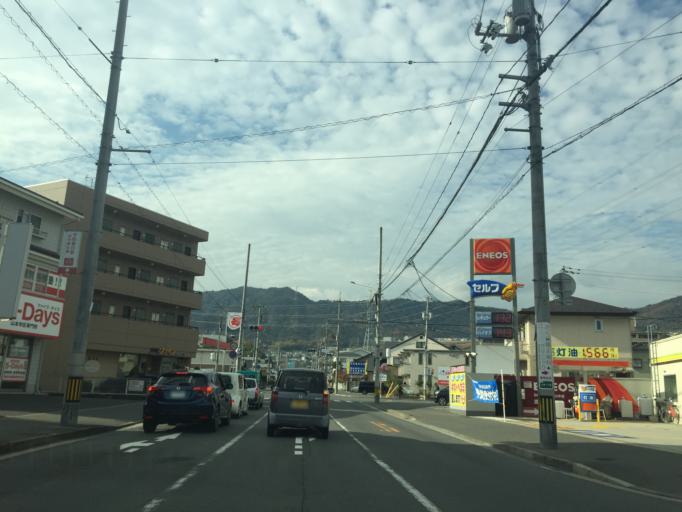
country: JP
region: Hiroshima
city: Hiroshima-shi
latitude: 34.4359
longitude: 132.4548
